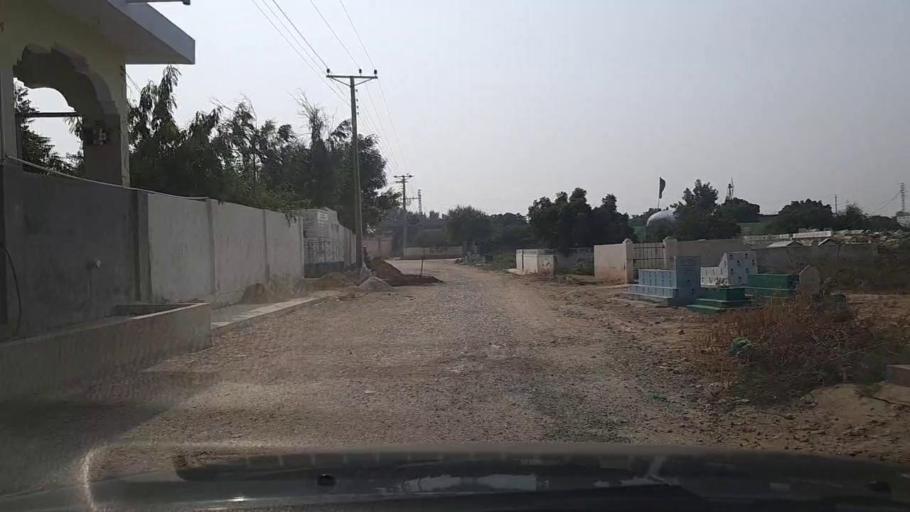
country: PK
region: Sindh
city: Thatta
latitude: 24.7466
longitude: 67.8984
